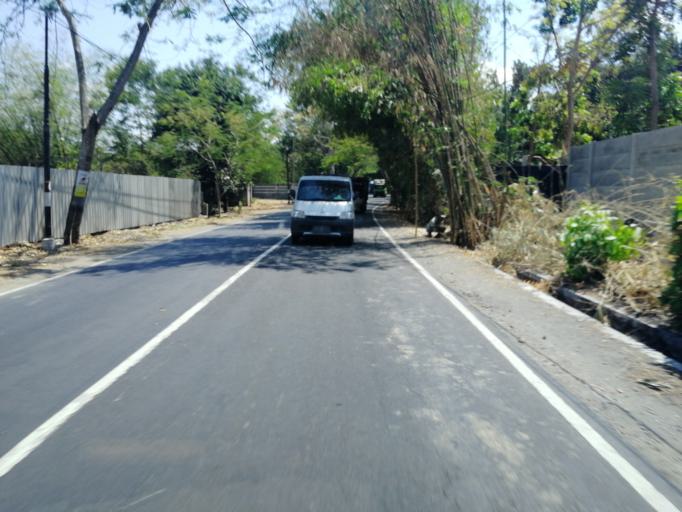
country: ID
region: West Nusa Tenggara
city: Jelateng Timur
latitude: -8.6950
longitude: 116.1077
